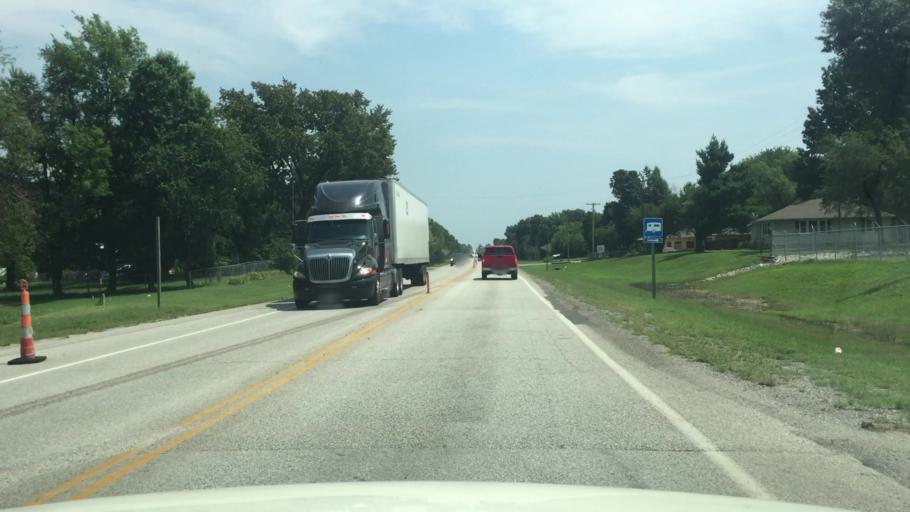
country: US
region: Kansas
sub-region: Cherokee County
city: Columbus
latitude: 37.1781
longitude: -94.8282
